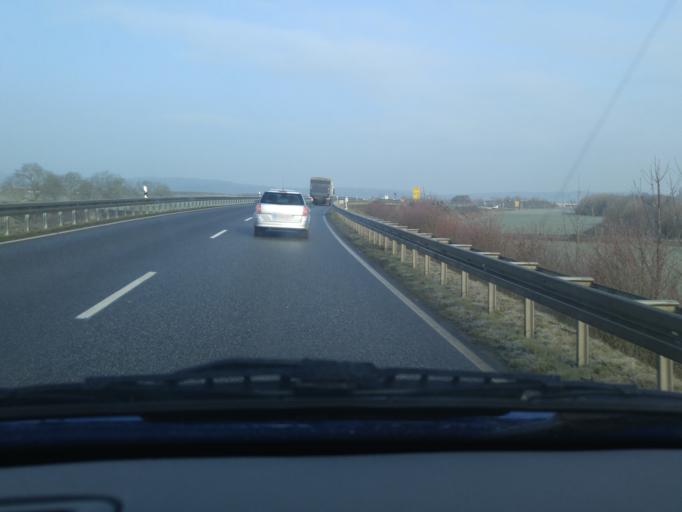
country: DE
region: Hesse
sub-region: Regierungsbezirk Darmstadt
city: Friedberg
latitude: 50.3181
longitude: 8.7372
